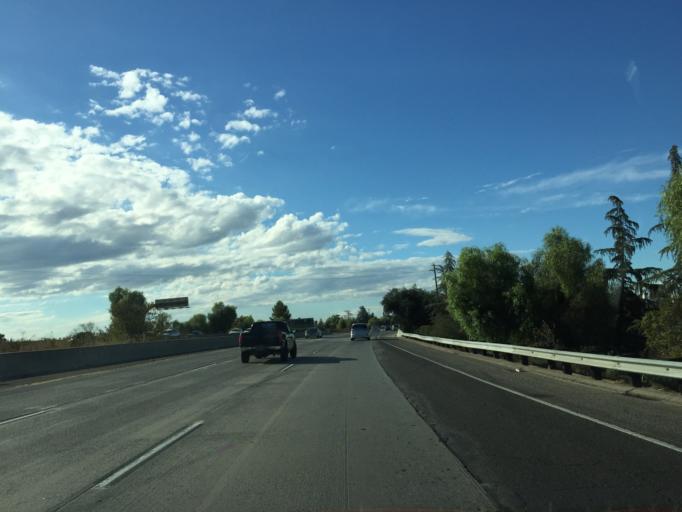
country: US
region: California
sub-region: Fresno County
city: Fresno
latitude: 36.7677
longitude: -119.7807
